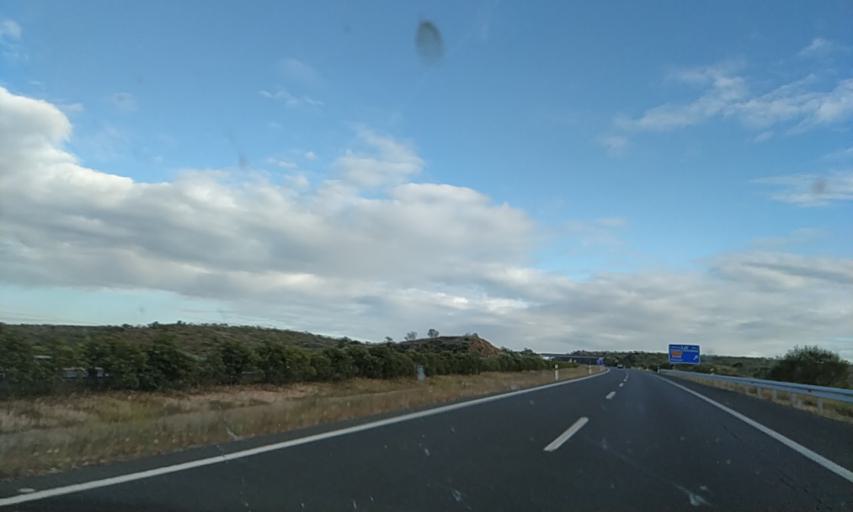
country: ES
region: Extremadura
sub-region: Provincia de Caceres
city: Hinojal
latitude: 39.7116
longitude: -6.4091
